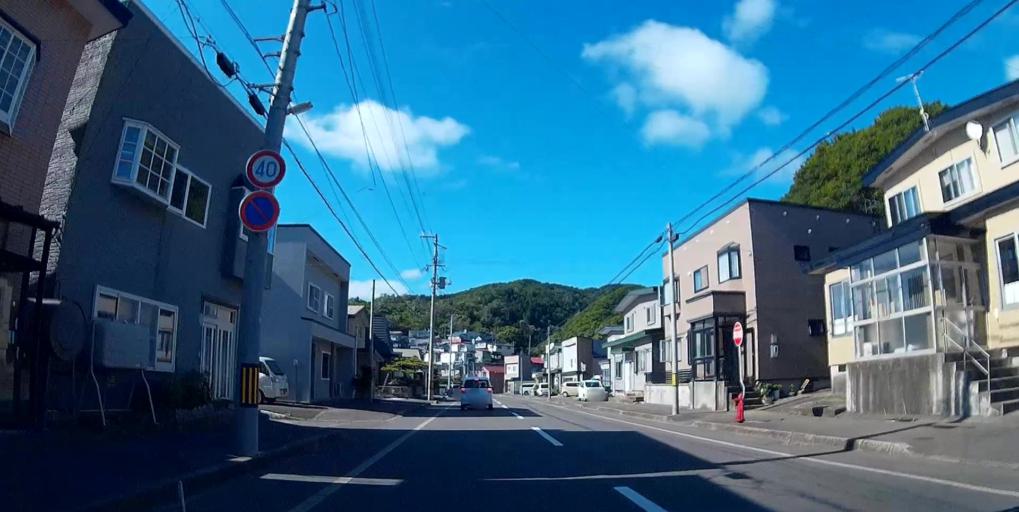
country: JP
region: Hokkaido
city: Kamiiso
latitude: 42.0456
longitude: 140.0848
